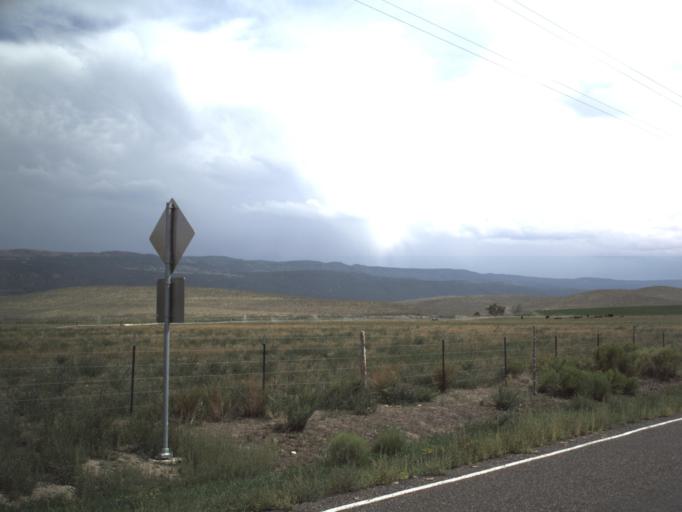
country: US
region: Utah
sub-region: Piute County
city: Junction
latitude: 38.0911
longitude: -111.9819
